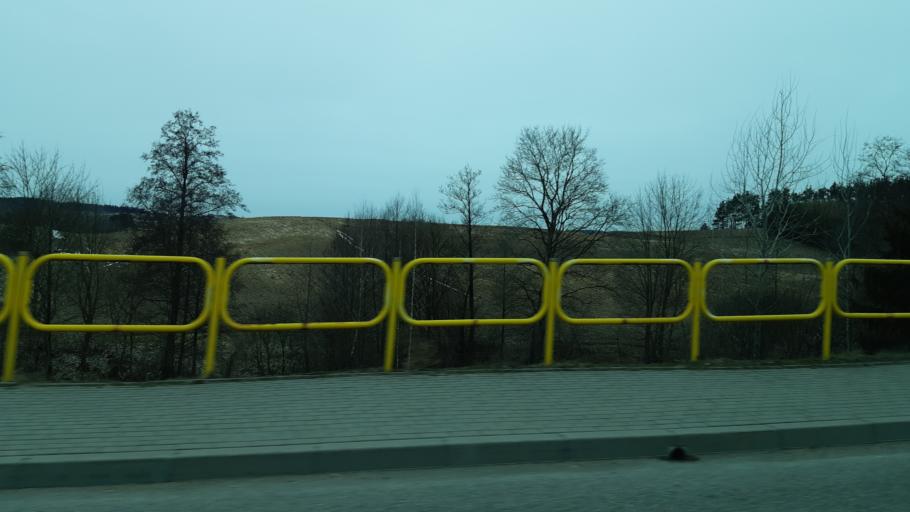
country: PL
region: Podlasie
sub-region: Suwalki
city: Suwalki
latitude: 54.3166
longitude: 22.9627
